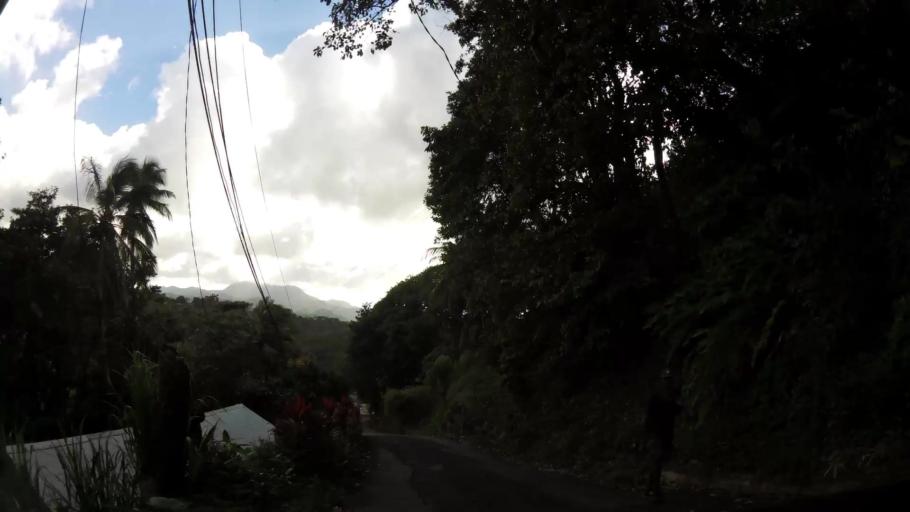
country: DM
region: Saint Andrew
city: Calibishie
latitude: 15.6021
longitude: -61.3964
